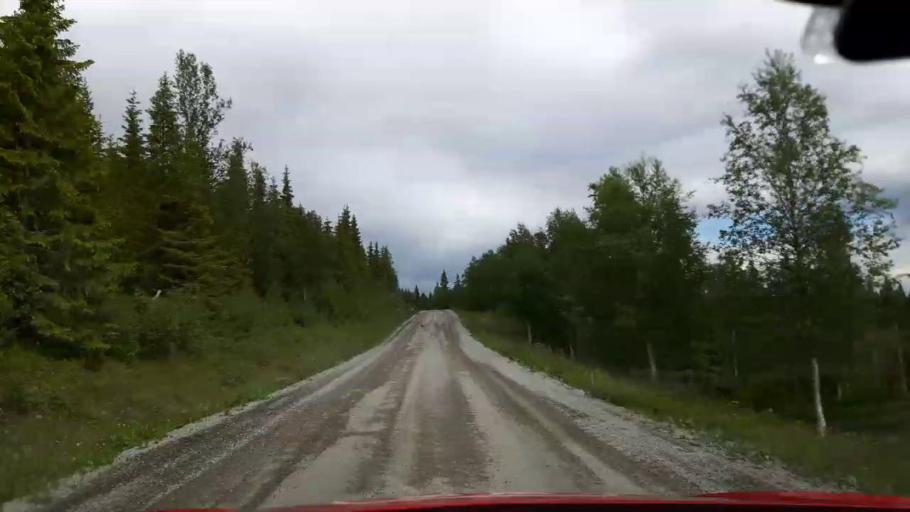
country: NO
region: Nord-Trondelag
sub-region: Lierne
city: Sandvika
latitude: 64.1442
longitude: 13.9352
